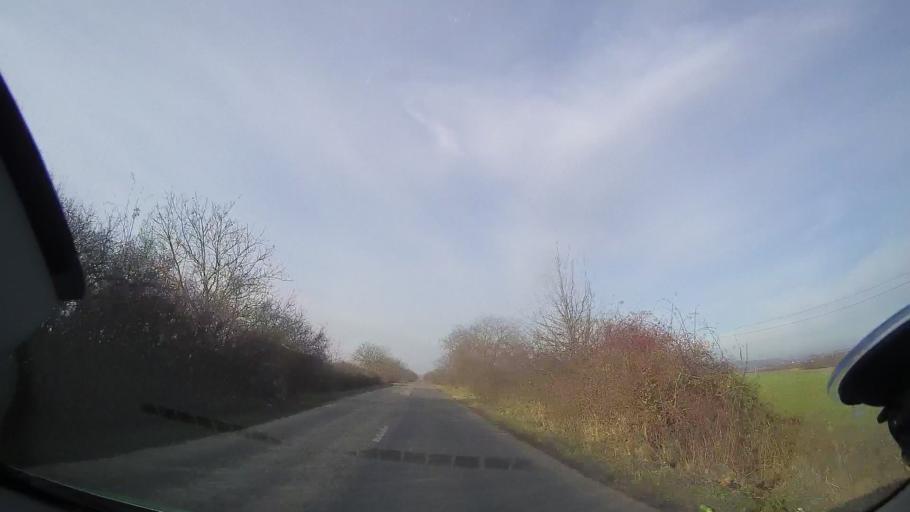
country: RO
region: Bihor
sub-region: Comuna Spinus
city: Spinus
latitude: 47.2154
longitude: 22.1758
